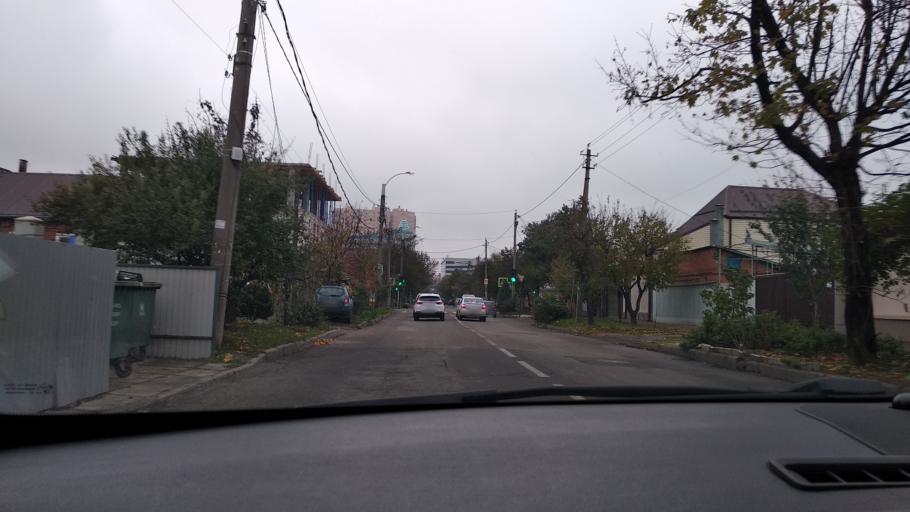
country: RU
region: Krasnodarskiy
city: Krasnodar
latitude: 45.0347
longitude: 38.9852
